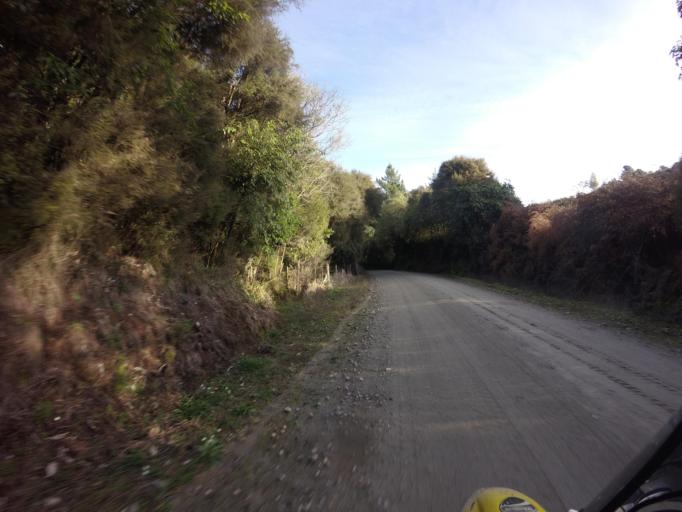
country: NZ
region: Hawke's Bay
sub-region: Wairoa District
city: Wairoa
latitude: -38.7510
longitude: 177.5255
